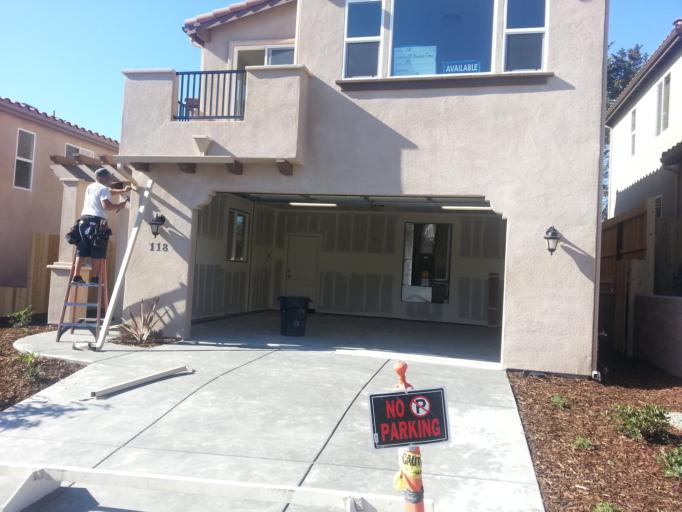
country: US
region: California
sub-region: San Luis Obispo County
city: Grover Beach
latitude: 35.1324
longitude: -120.6097
